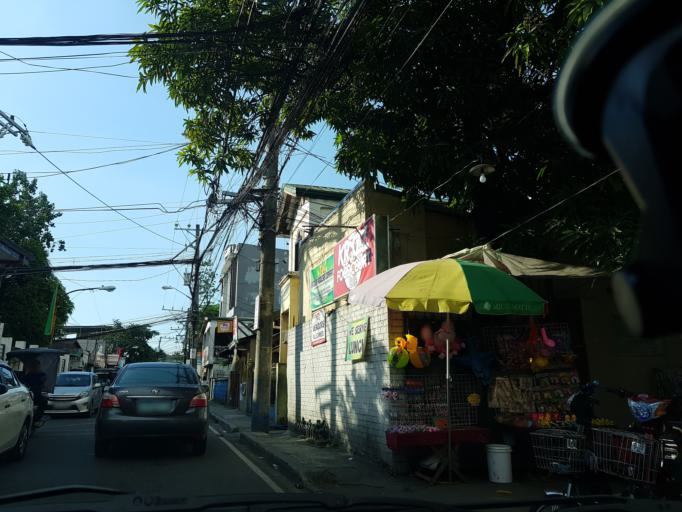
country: PH
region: Metro Manila
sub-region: Marikina
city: Calumpang
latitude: 14.6142
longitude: 121.0826
